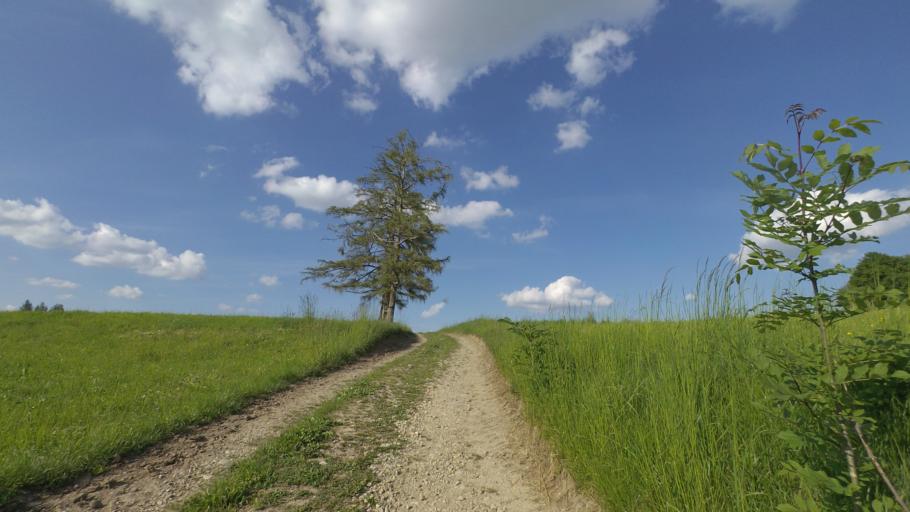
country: DE
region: Bavaria
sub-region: Upper Bavaria
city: Nussdorf
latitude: 47.8865
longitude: 12.6049
